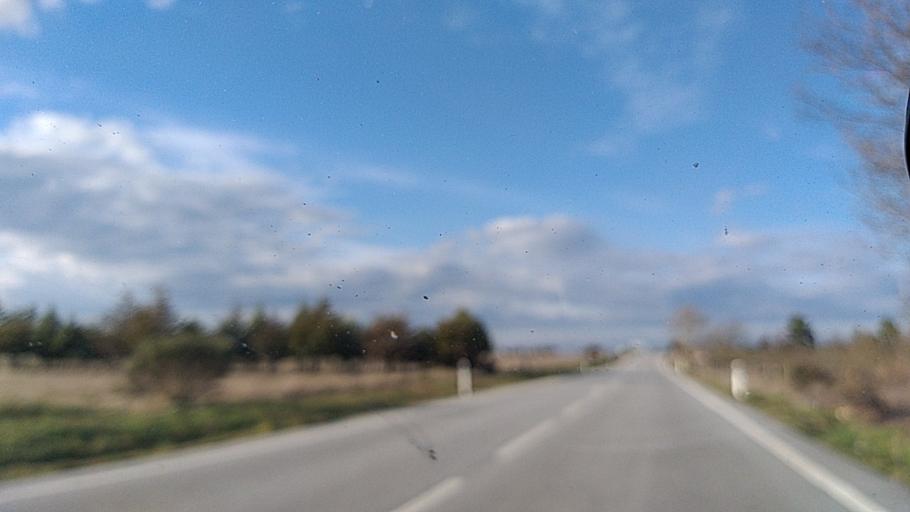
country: ES
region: Castille and Leon
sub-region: Provincia de Salamanca
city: Fuentes de Onoro
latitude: 40.6541
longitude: -6.8573
